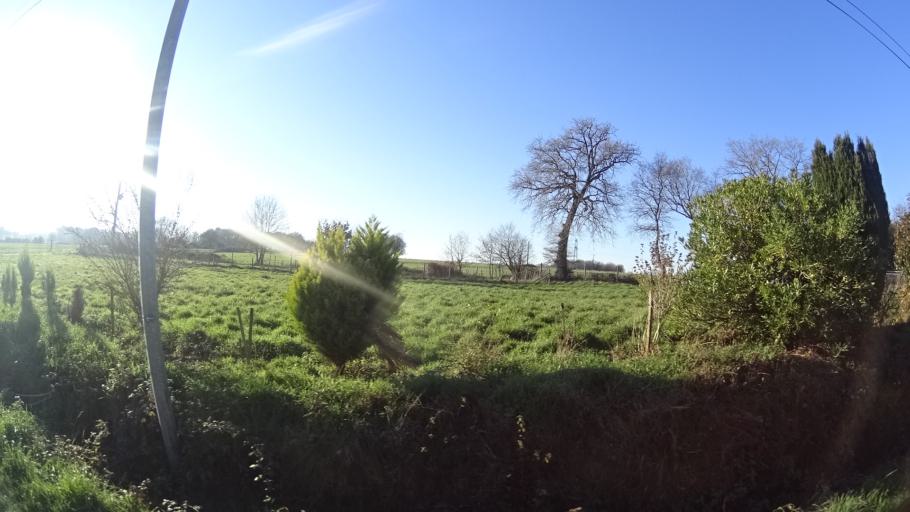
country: FR
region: Brittany
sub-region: Departement du Morbihan
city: Saint-Jacut-les-Pins
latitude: 47.6678
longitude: -2.1937
